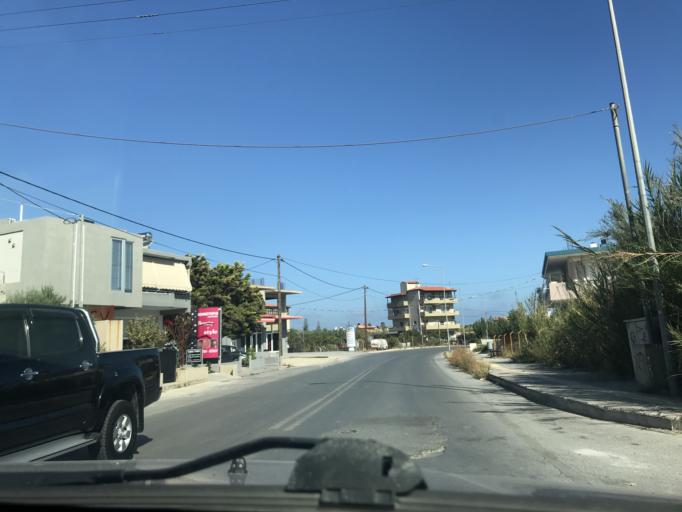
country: GR
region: Crete
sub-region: Nomos Irakleiou
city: Gazi
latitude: 35.3307
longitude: 25.0642
